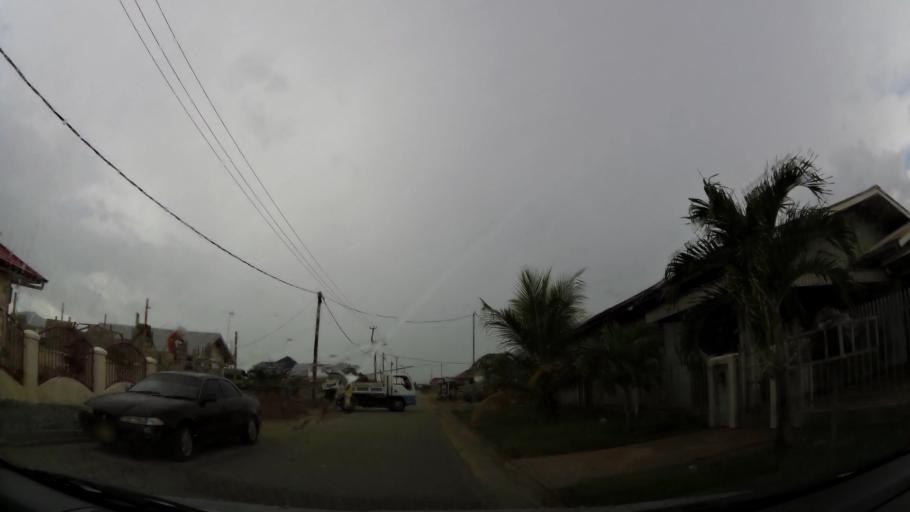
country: SR
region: Commewijne
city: Nieuw Amsterdam
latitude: 5.8558
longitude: -55.1175
